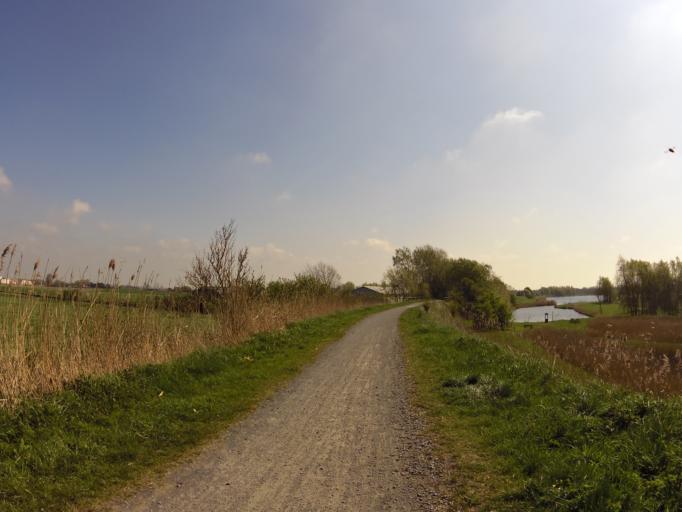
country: BE
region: Flanders
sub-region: Provincie West-Vlaanderen
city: Nieuwpoort
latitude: 51.1248
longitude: 2.7550
